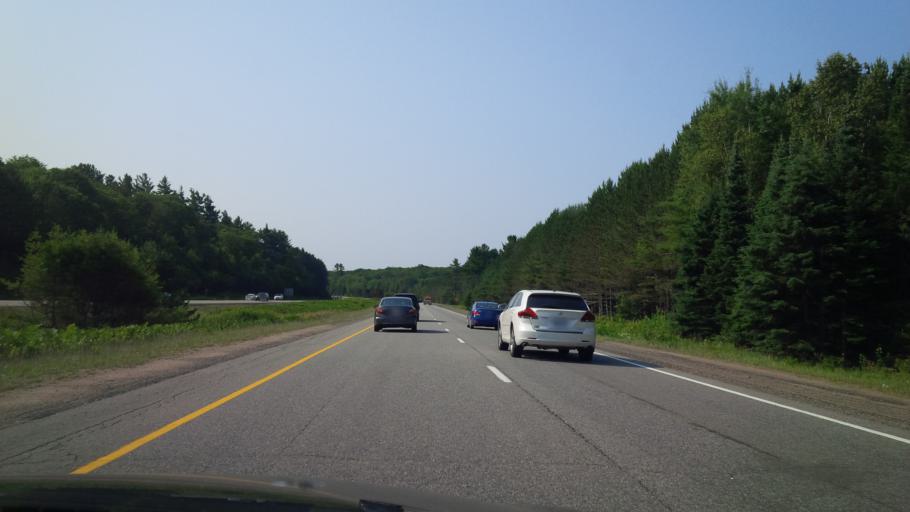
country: CA
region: Ontario
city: Bracebridge
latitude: 45.1107
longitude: -79.3109
